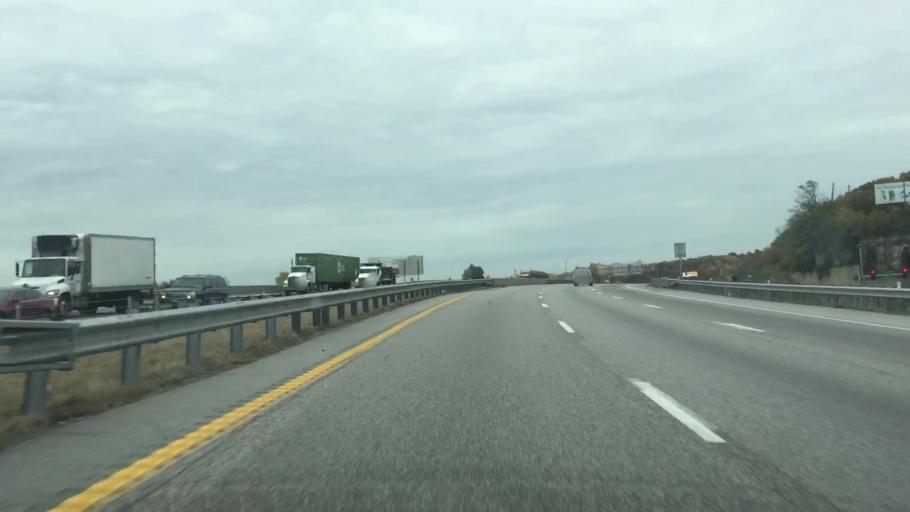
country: US
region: Missouri
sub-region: Jackson County
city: Sugar Creek
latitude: 39.0814
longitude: -94.4908
